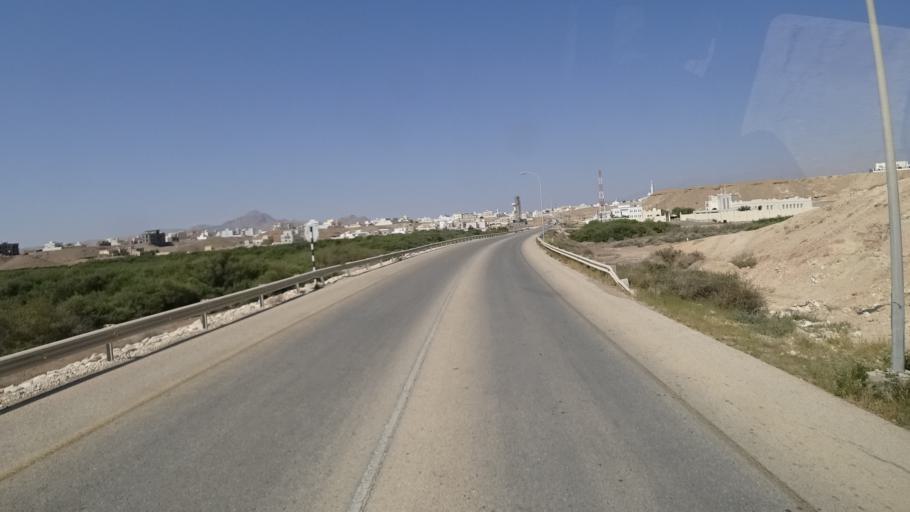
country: OM
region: Ash Sharqiyah
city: Sur
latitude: 22.5629
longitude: 59.5080
